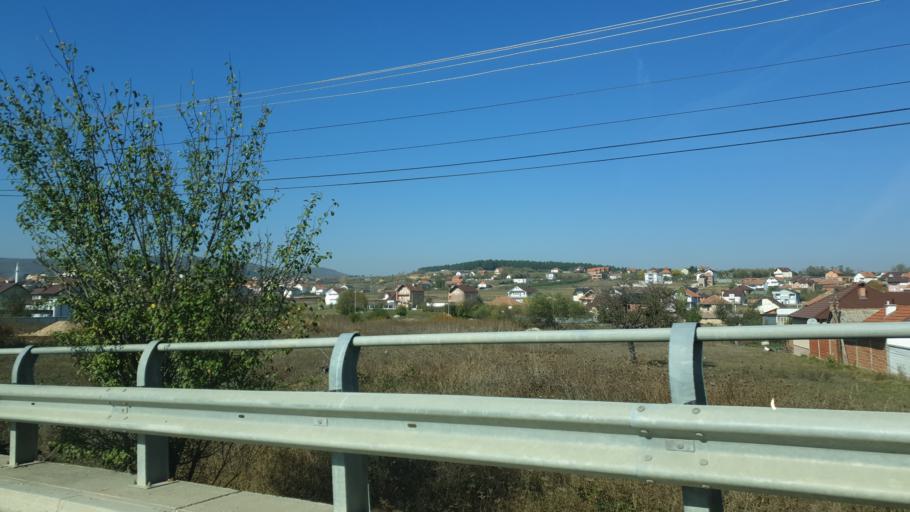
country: XK
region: Pristina
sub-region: Komuna e Gracanices
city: Glanica
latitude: 42.6006
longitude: 21.0267
